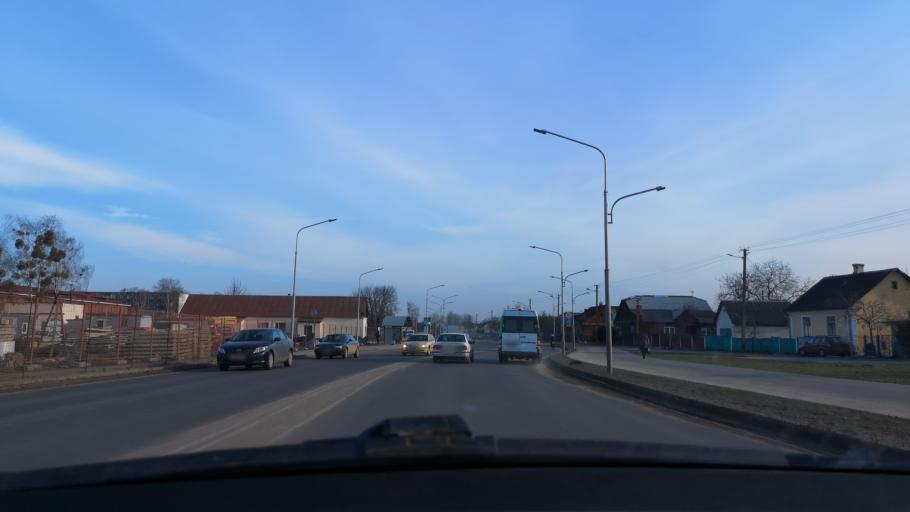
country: BY
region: Brest
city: Brest
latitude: 52.1042
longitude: 23.6669
